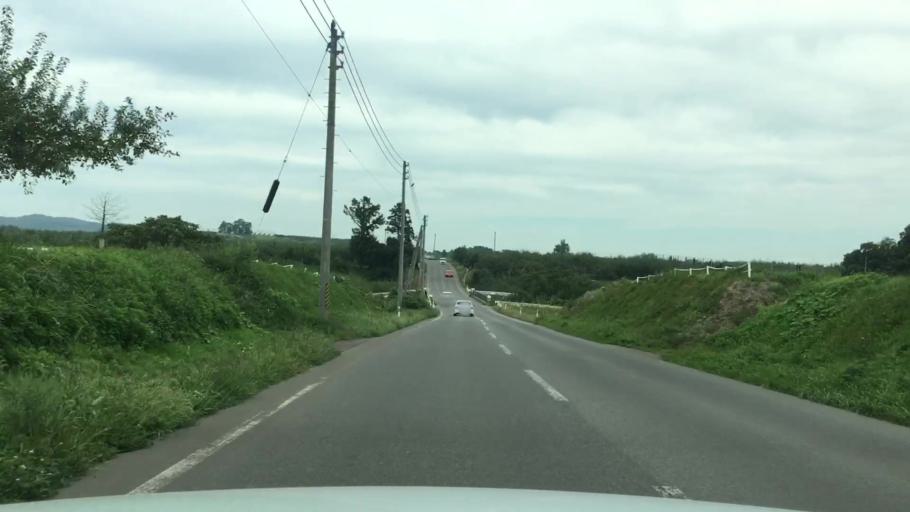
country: JP
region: Aomori
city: Hirosaki
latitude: 40.6547
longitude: 140.4209
